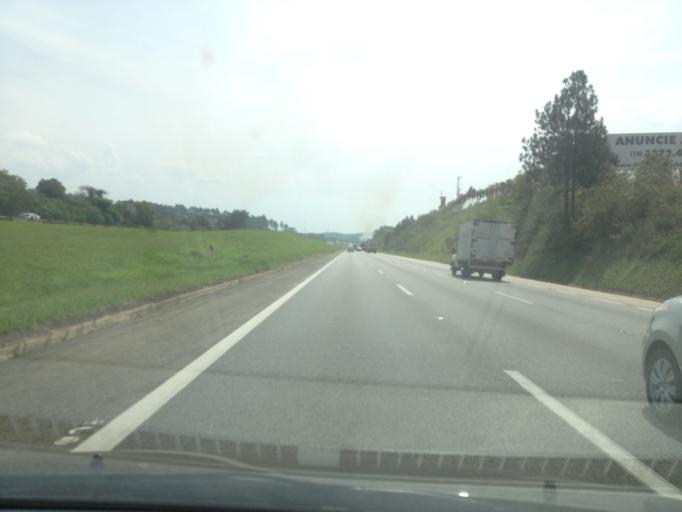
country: BR
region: Sao Paulo
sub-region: Sao Roque
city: Sao Roque
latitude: -23.4197
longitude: -47.1954
